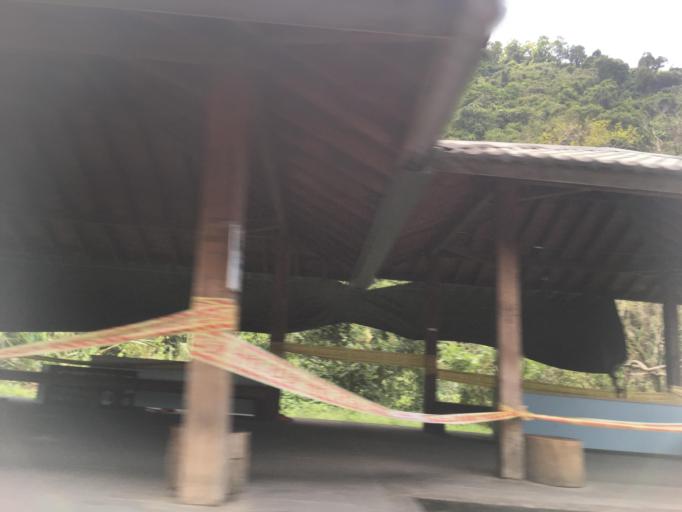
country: TW
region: Taiwan
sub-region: Yilan
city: Yilan
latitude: 24.6066
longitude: 121.7471
